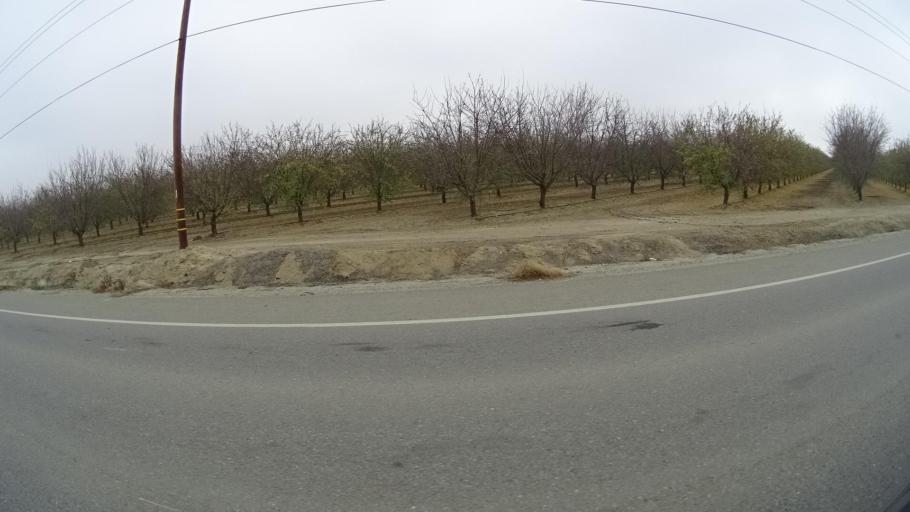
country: US
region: California
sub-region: Kern County
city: Greenfield
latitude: 35.0872
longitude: -119.1162
